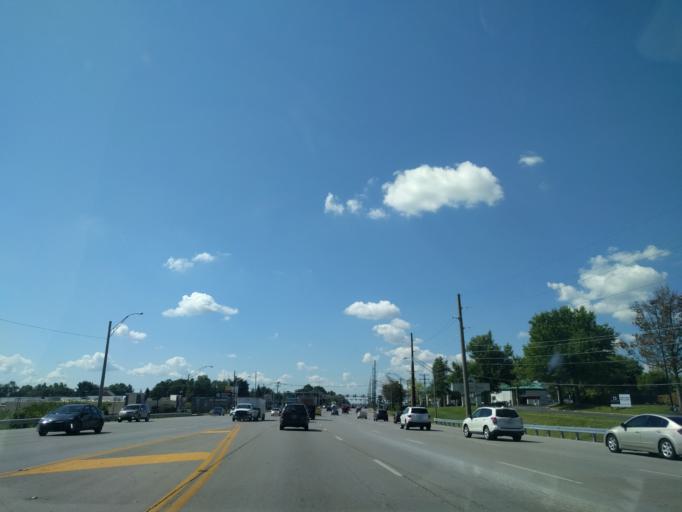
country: US
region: Kentucky
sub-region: Fayette County
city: Monticello
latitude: 37.9943
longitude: -84.5224
